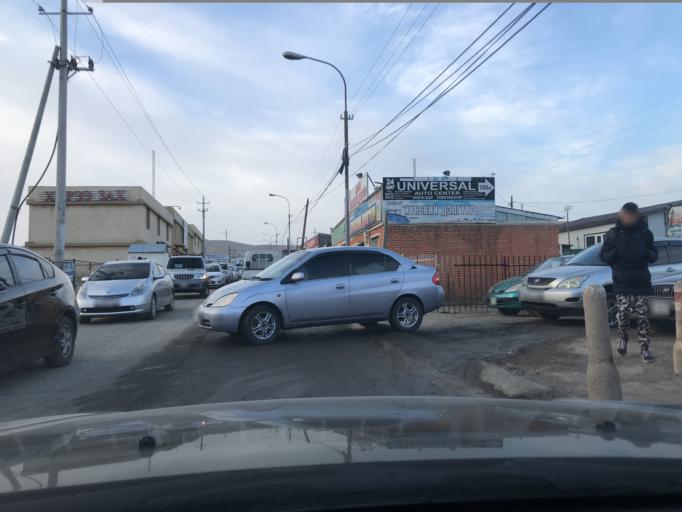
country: MN
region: Ulaanbaatar
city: Ulaanbaatar
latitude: 47.9274
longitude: 106.9982
